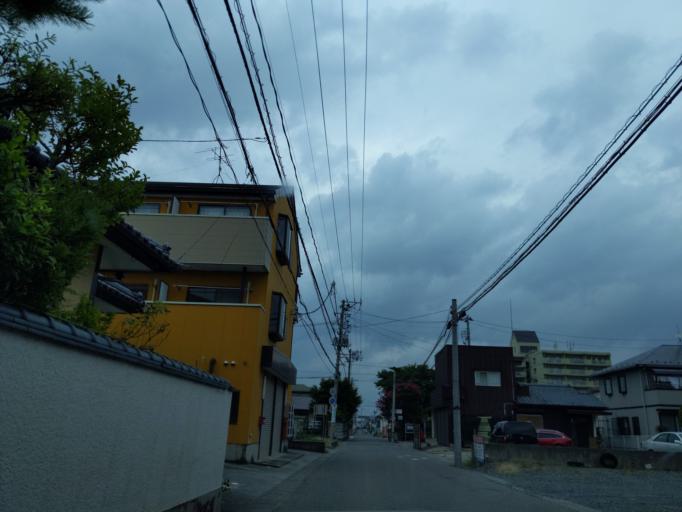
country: JP
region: Fukushima
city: Koriyama
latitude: 37.3934
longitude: 140.3425
